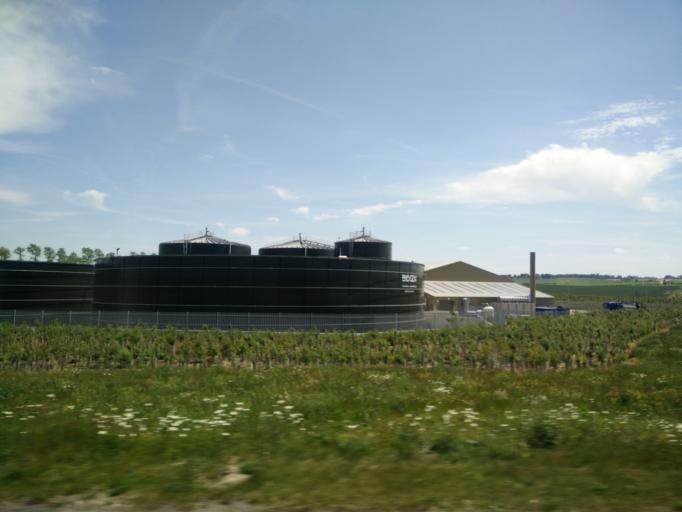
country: GB
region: England
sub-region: Hertfordshire
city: Baldock
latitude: 52.0042
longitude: -0.1443
